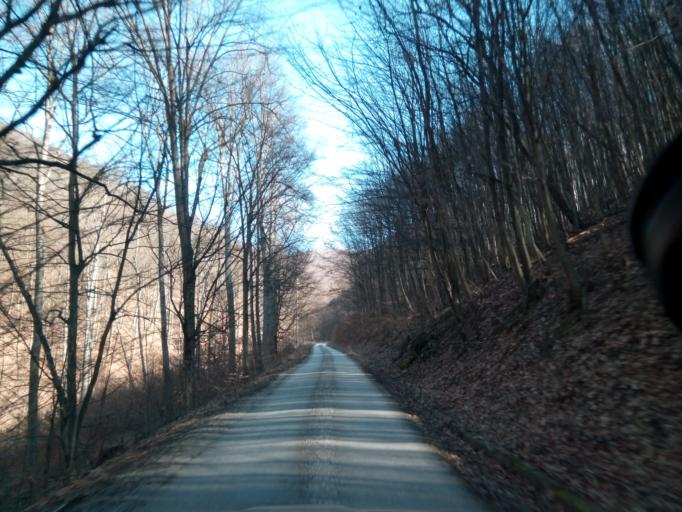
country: SK
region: Kosicky
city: Roznava
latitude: 48.5530
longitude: 20.5700
